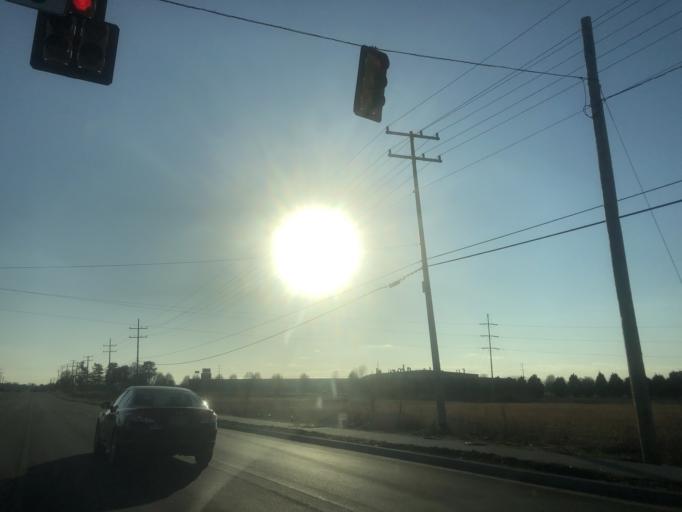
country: US
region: Tennessee
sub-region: Sumner County
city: Portland
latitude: 36.6328
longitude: -86.5643
